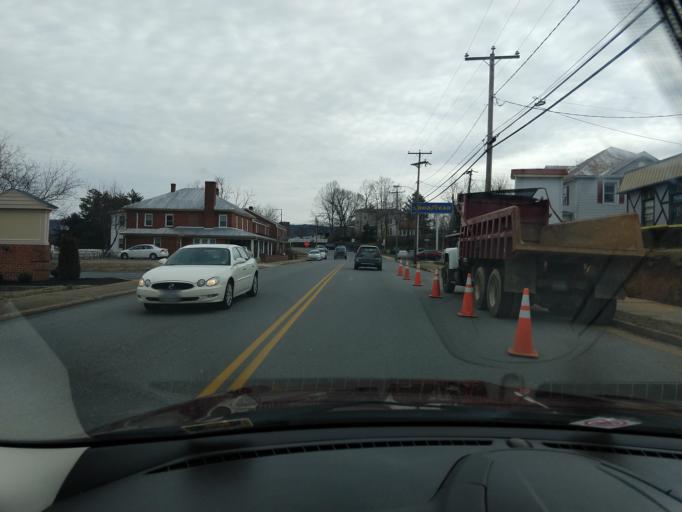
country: US
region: Virginia
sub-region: City of Waynesboro
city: Waynesboro
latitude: 38.0699
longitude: -78.8955
